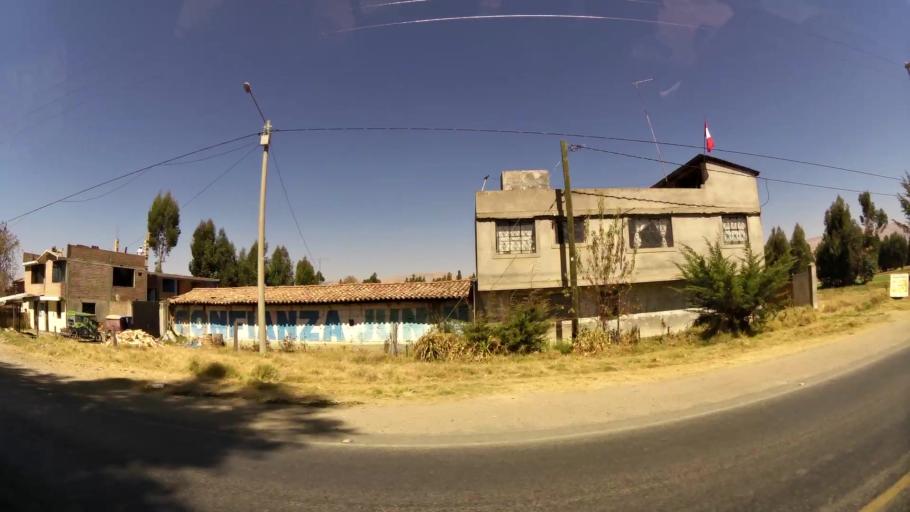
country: PE
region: Junin
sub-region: Provincia de Concepcion
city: Matahuasi
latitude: -11.8788
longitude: -75.3592
